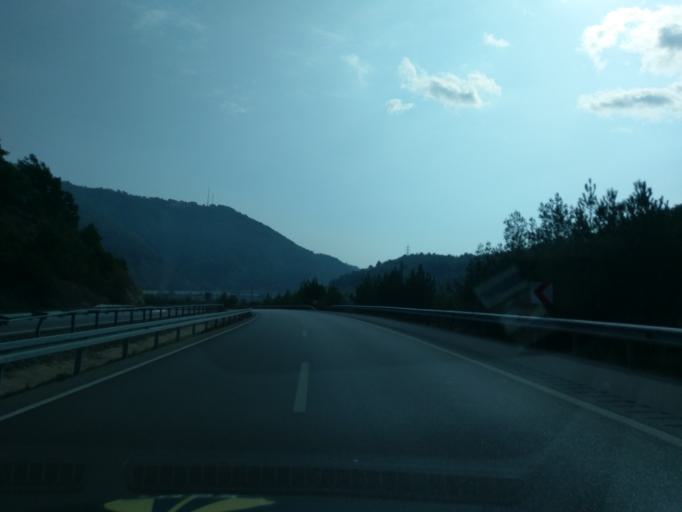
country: TR
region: Amasya
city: Akdag
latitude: 40.7517
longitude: 36.0766
